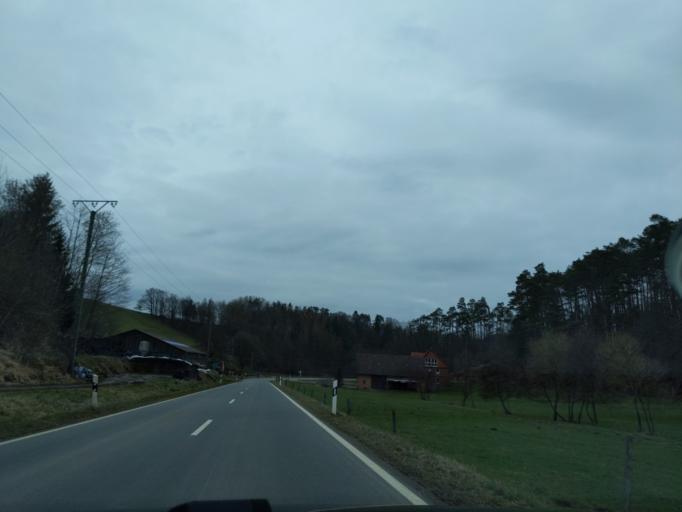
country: DE
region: Hesse
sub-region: Regierungsbezirk Kassel
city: Bad Arolsen
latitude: 51.3335
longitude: 9.0716
